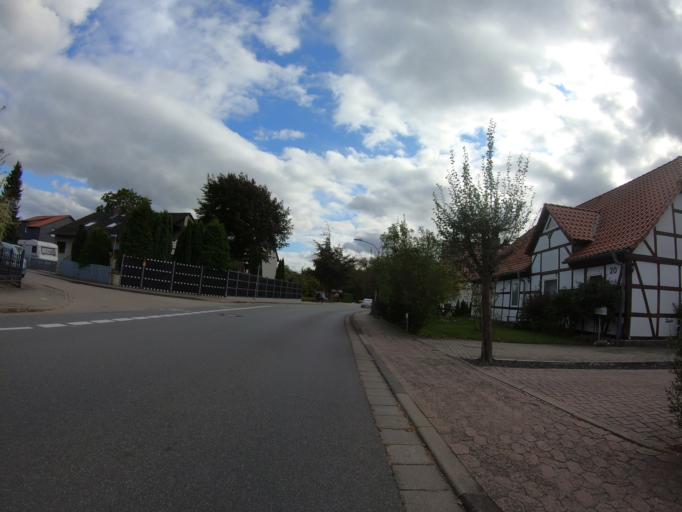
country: DE
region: Lower Saxony
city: Wasbuttel
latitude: 52.4140
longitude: 10.5921
